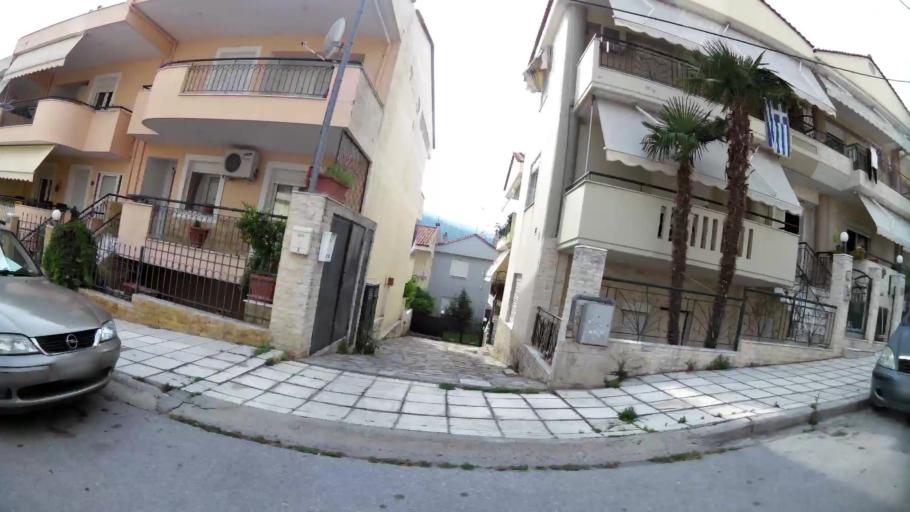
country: GR
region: Central Macedonia
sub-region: Nomos Thessalonikis
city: Oraiokastro
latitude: 40.7288
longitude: 22.9133
